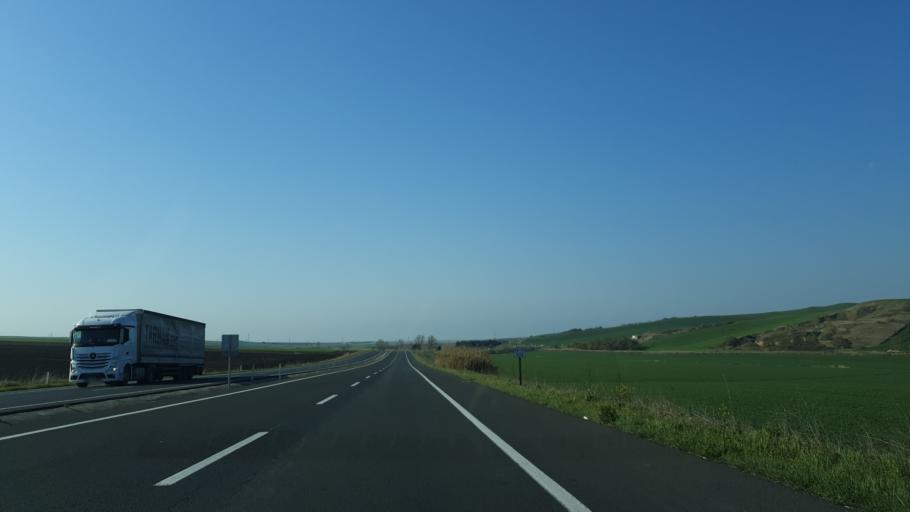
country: TR
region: Tekirdag
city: Corlu
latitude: 41.0587
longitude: 27.7382
